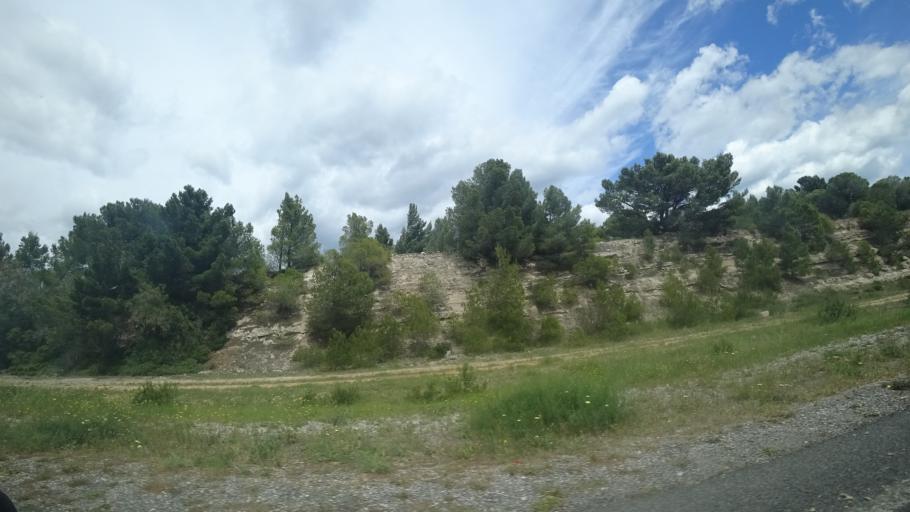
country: FR
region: Languedoc-Roussillon
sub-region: Departement de l'Aude
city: Leucate
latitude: 42.9168
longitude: 3.0212
